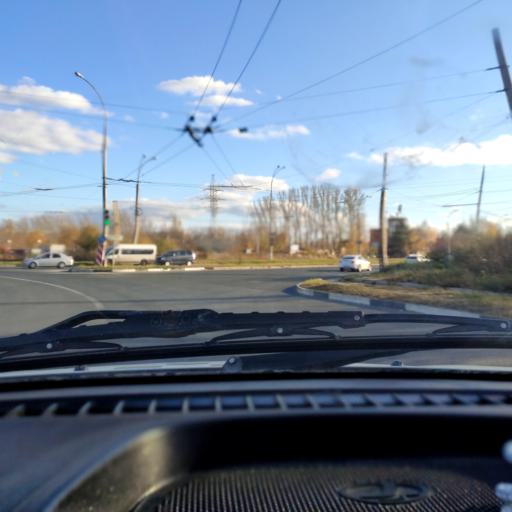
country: RU
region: Samara
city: Tol'yatti
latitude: 53.5518
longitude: 49.3024
